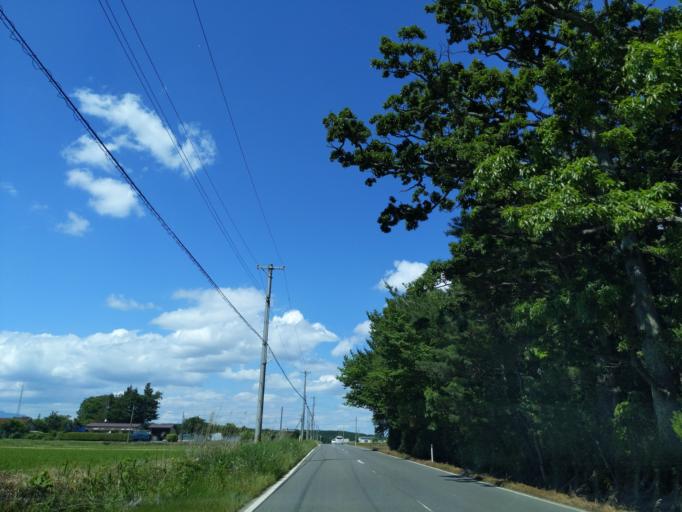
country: JP
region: Fukushima
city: Koriyama
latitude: 37.3791
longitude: 140.2955
